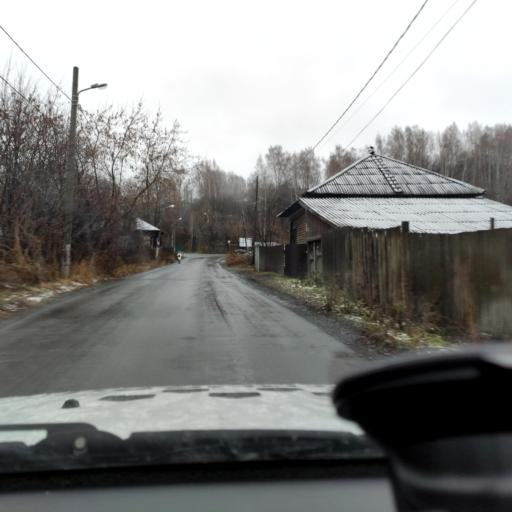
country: RU
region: Perm
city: Perm
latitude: 58.0572
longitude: 56.3336
